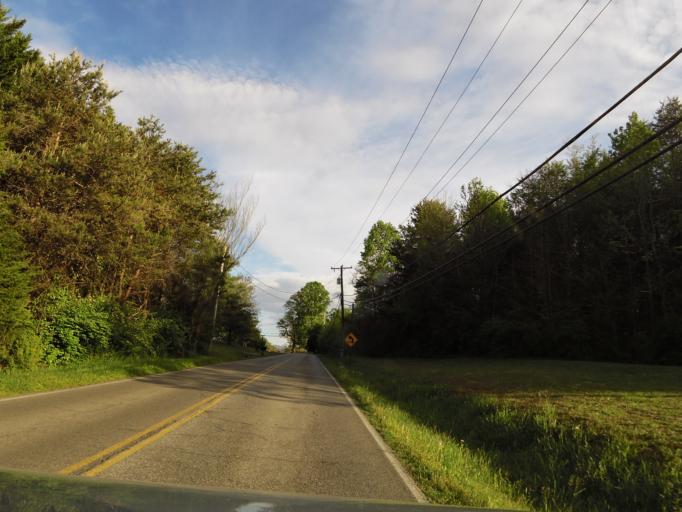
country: US
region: Tennessee
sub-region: Blount County
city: Maryville
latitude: 35.6963
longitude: -84.0245
